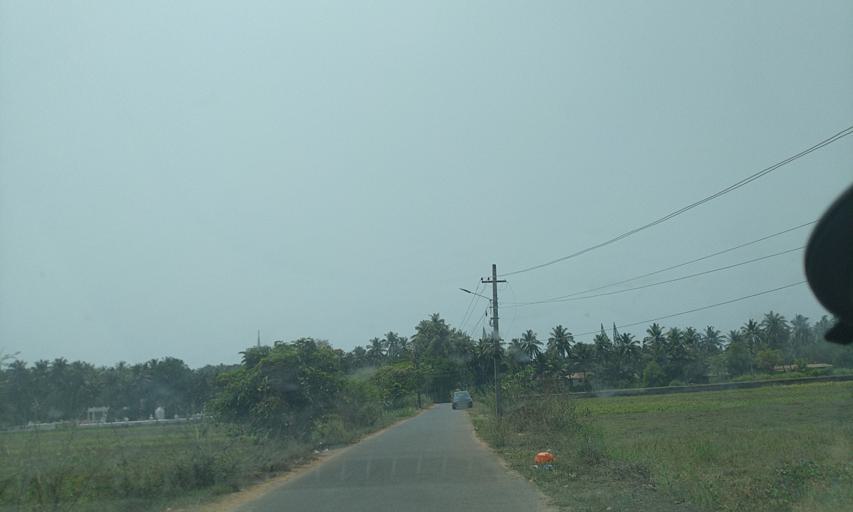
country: IN
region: Goa
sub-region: North Goa
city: Saligao
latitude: 15.5476
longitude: 73.7873
